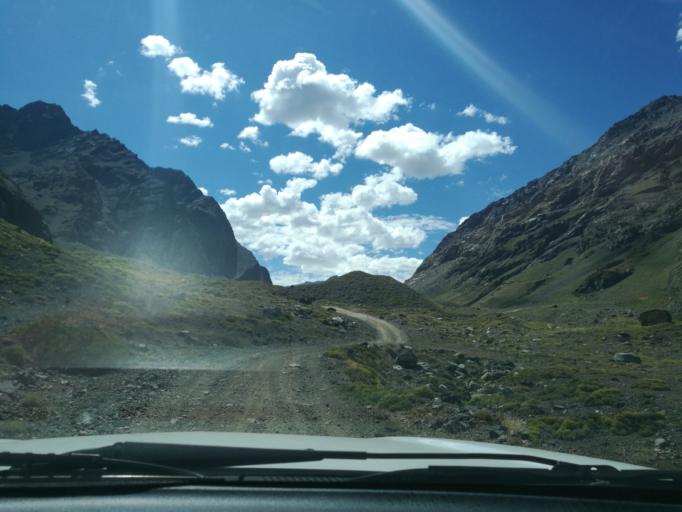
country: CL
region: O'Higgins
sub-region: Provincia de Cachapoal
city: Machali
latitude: -34.4115
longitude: -70.2316
